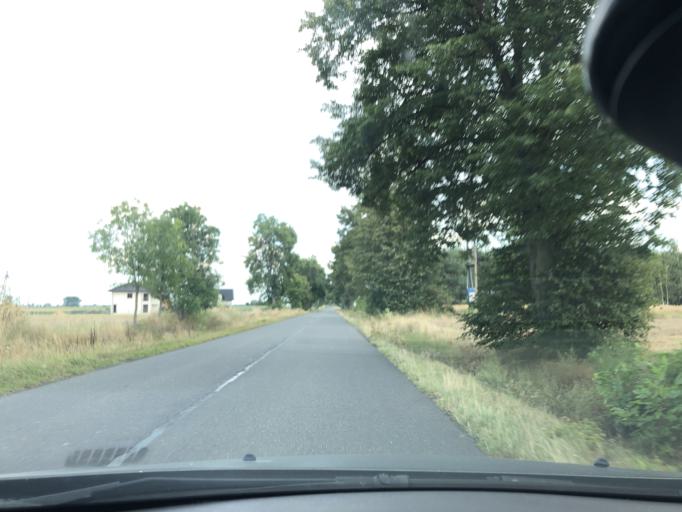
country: PL
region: Lodz Voivodeship
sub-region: Powiat wieruszowski
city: Walichnowy
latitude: 51.2399
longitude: 18.3743
